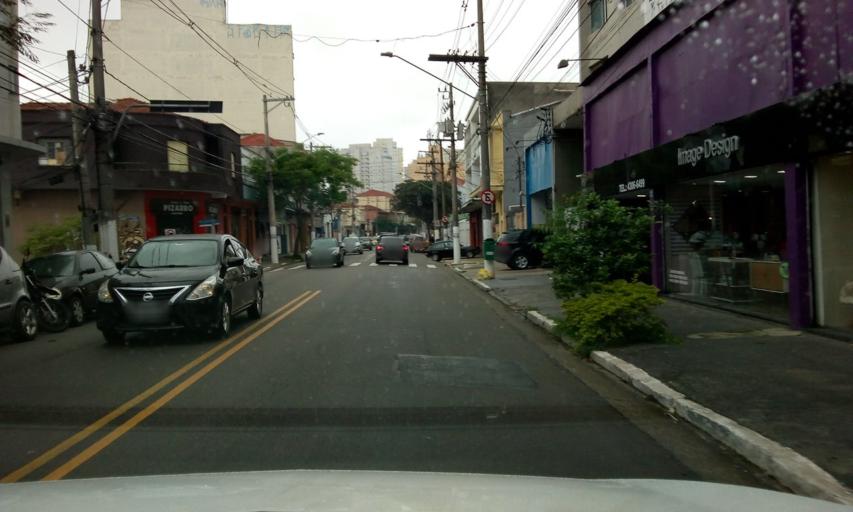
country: BR
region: Sao Paulo
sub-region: Sao Paulo
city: Sao Paulo
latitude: -23.5841
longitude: -46.6277
